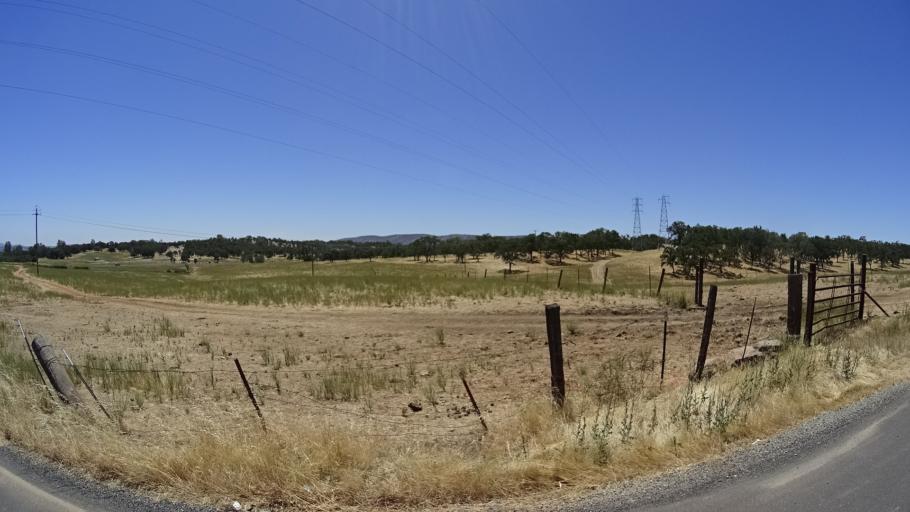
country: US
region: California
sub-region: Calaveras County
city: Copperopolis
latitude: 37.9741
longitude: -120.6600
